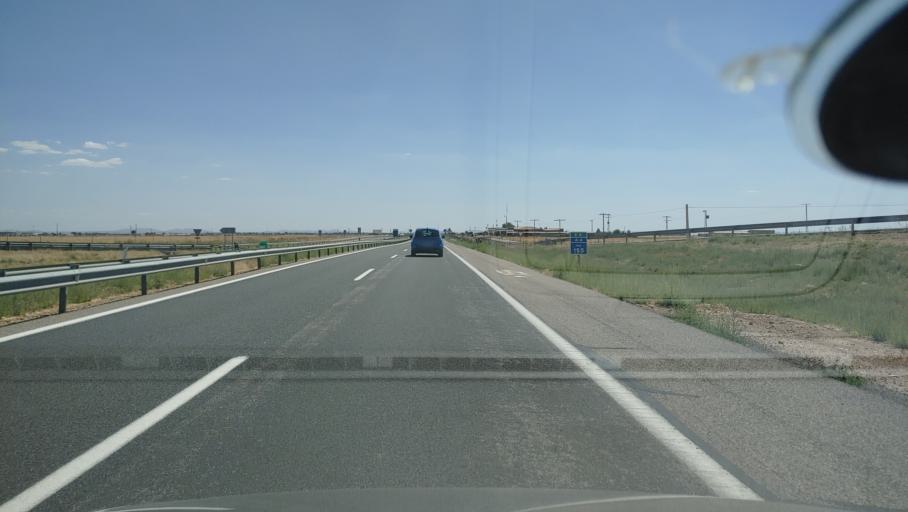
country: ES
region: Castille-La Mancha
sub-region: Provincia de Ciudad Real
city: Villarta de San Juan
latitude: 39.1668
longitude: -3.3930
